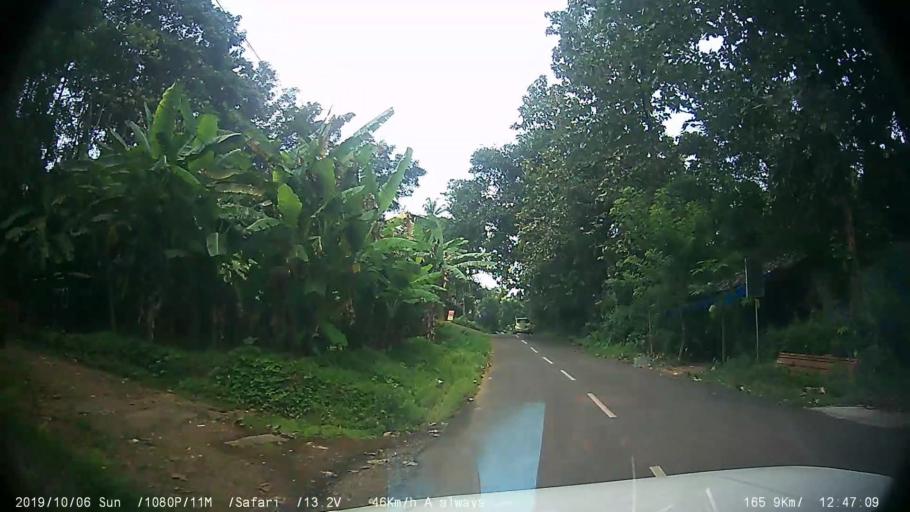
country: IN
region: Kerala
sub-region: Kottayam
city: Palackattumala
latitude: 9.7730
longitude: 76.6031
